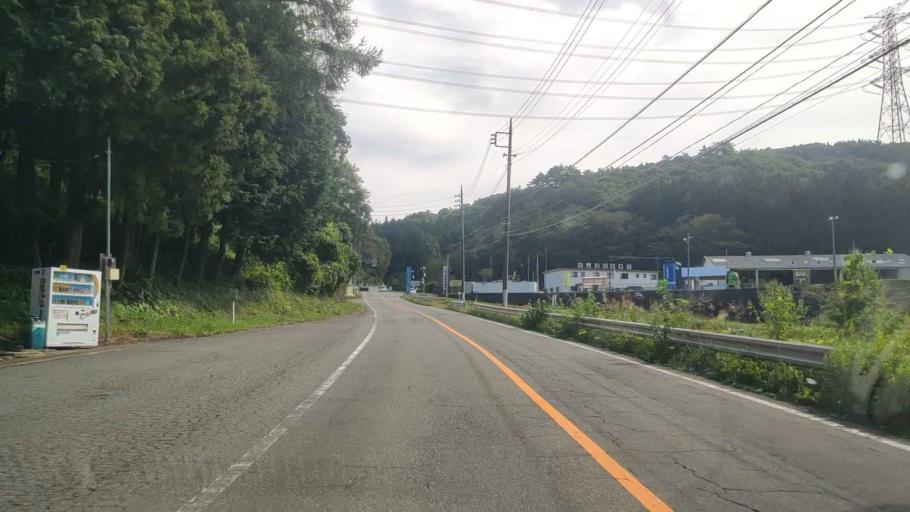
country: JP
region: Gunma
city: Numata
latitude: 36.6296
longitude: 138.9818
